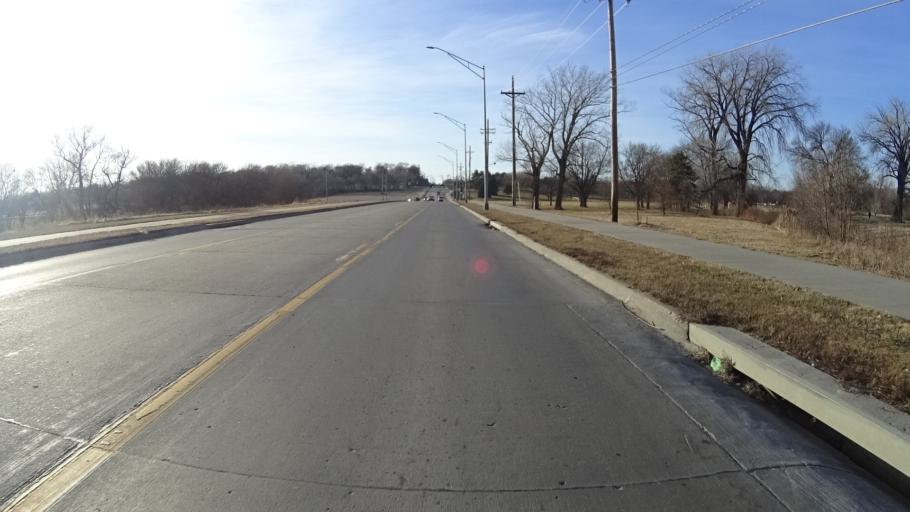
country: US
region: Nebraska
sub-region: Sarpy County
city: La Vista
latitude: 41.1908
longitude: -96.0116
